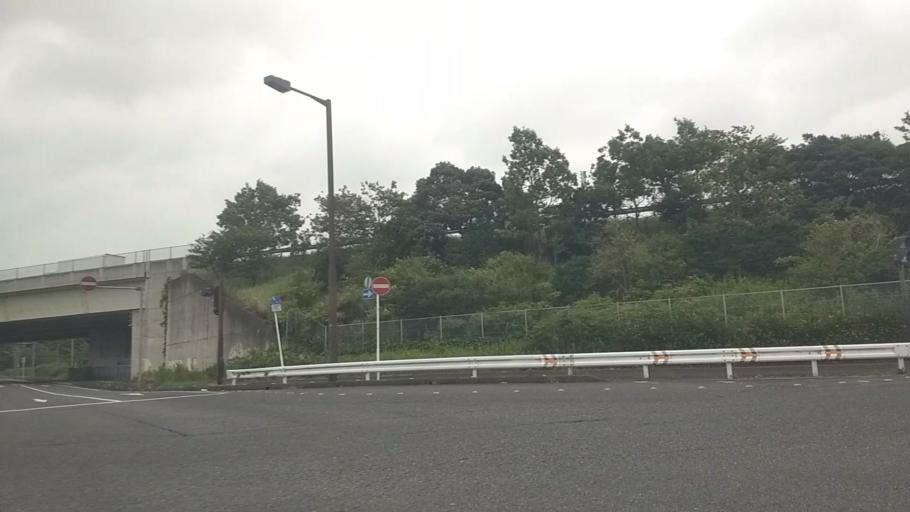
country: JP
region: Chiba
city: Kisarazu
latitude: 35.3880
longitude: 139.9703
